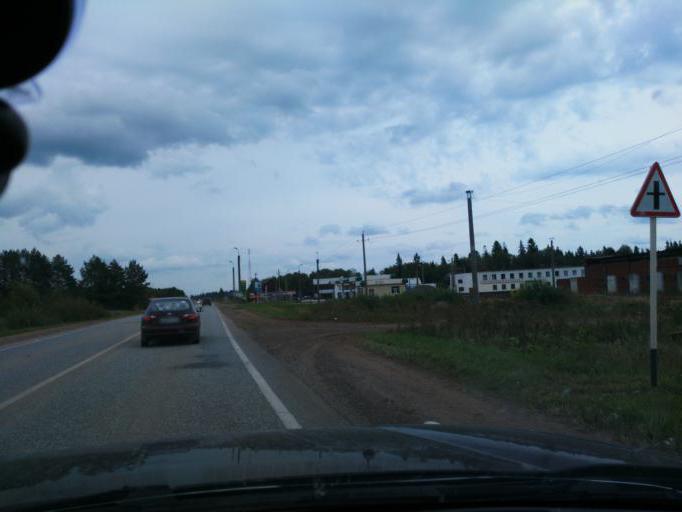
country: RU
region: Perm
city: Chernushka
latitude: 56.5337
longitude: 56.0652
